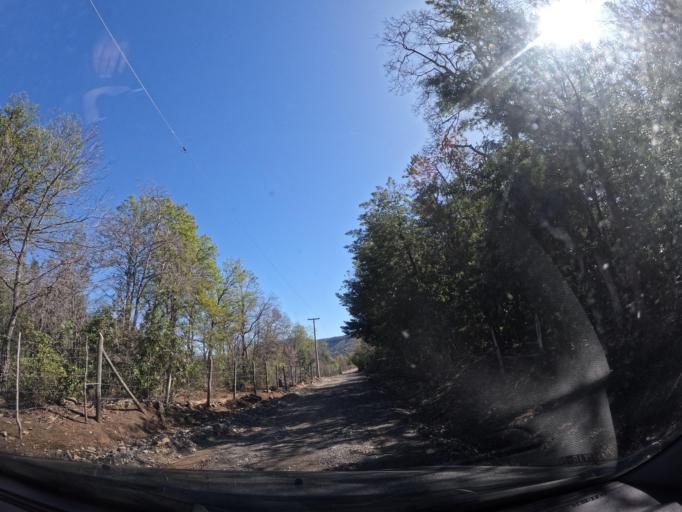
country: CL
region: Maule
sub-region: Provincia de Linares
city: Longavi
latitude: -36.2397
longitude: -71.3535
